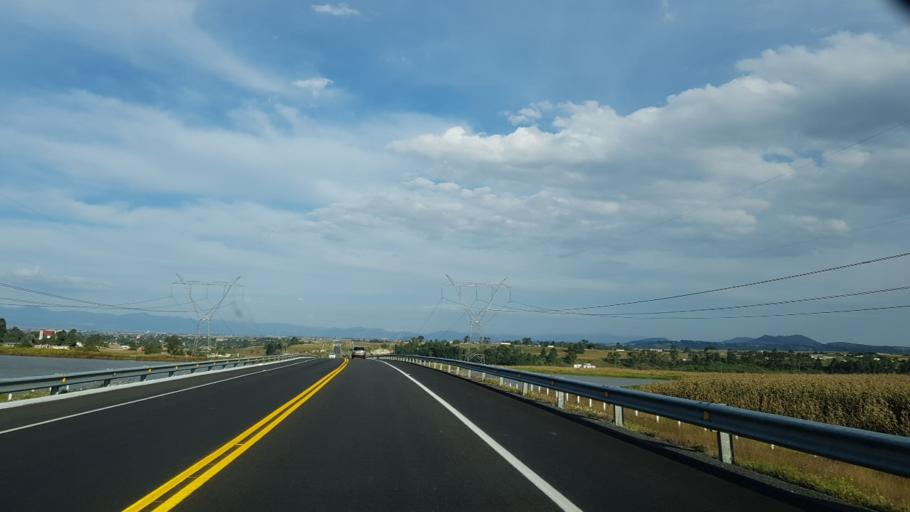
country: MX
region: Mexico
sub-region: Almoloya de Juarez
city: San Pedro de la Hortaliza (Ejido Almoloyan)
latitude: 19.3777
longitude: -99.8471
